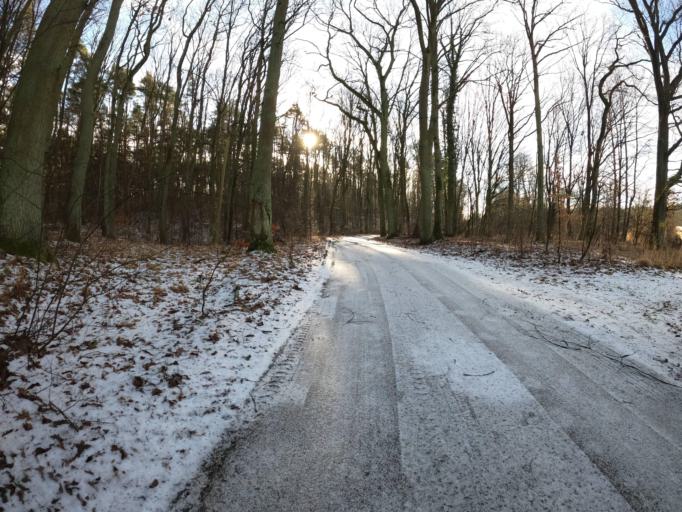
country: PL
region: Lubusz
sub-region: Powiat slubicki
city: Rzepin
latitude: 52.3059
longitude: 14.8129
